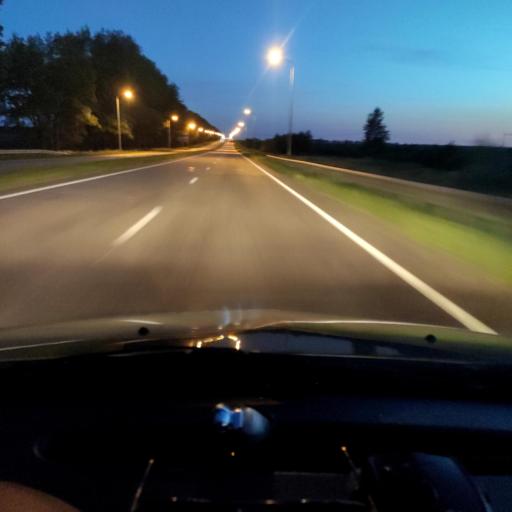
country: RU
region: Belgorod
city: Skorodnoye
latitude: 51.1809
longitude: 37.3479
